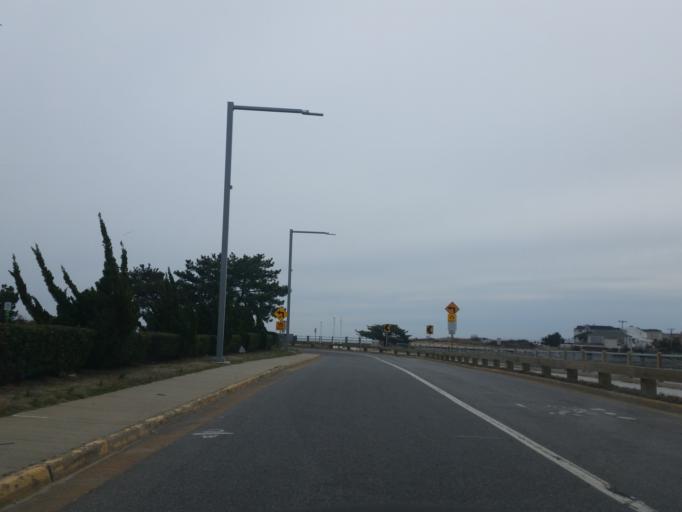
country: US
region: Virginia
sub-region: City of Virginia Beach
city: Virginia Beach
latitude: 36.8308
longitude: -75.9713
